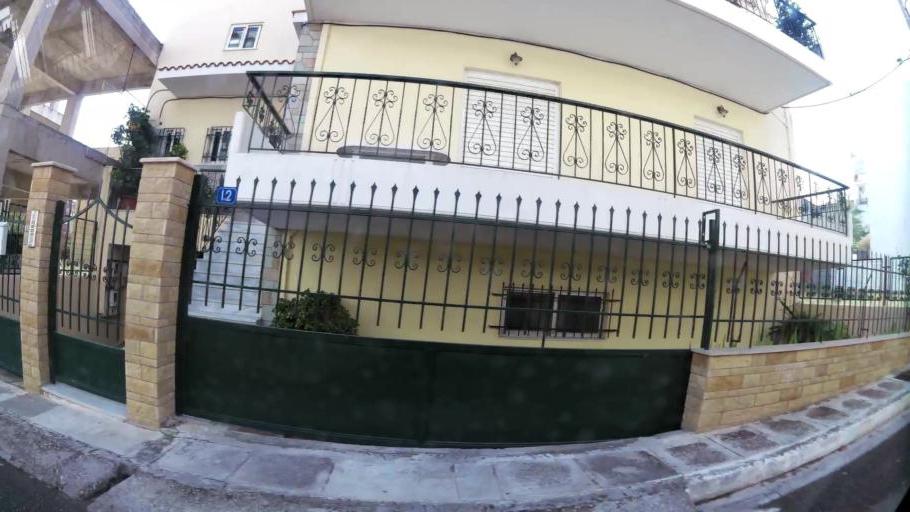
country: GR
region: Attica
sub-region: Nomarchia Dytikis Attikis
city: Zefyri
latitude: 38.0661
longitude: 23.7189
